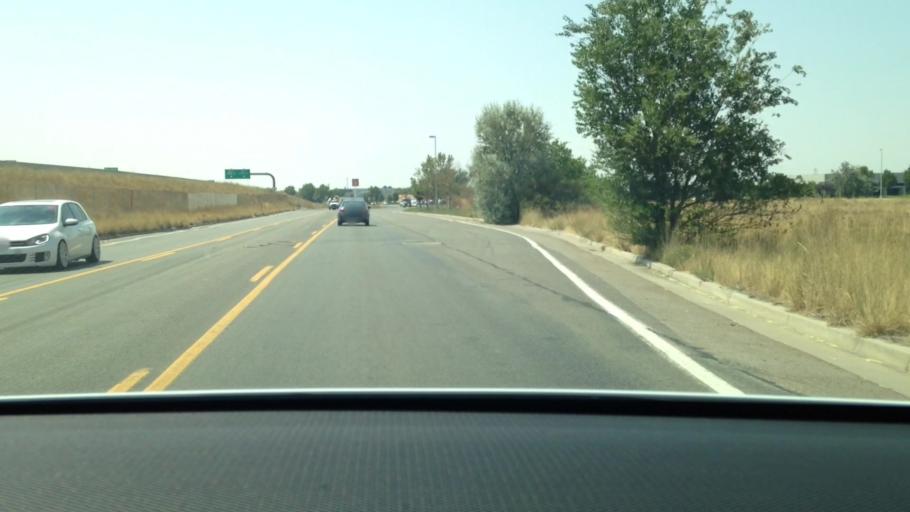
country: US
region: Utah
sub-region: Salt Lake County
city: West Valley City
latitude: 40.7269
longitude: -111.9632
